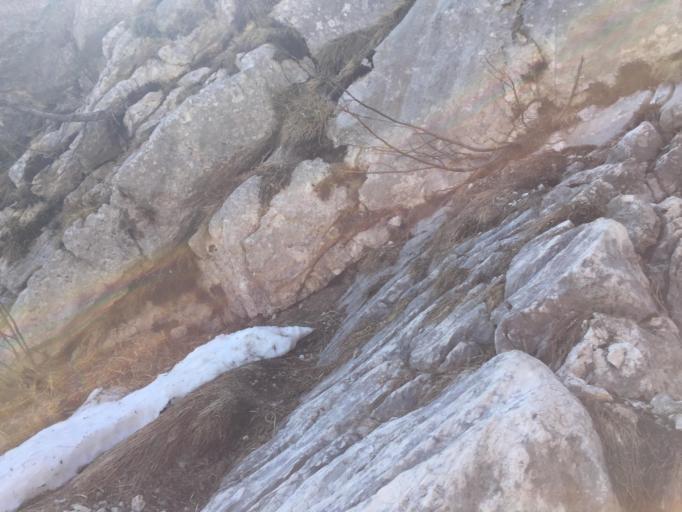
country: IT
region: Friuli Venezia Giulia
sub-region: Provincia di Udine
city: Amaro
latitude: 46.3983
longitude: 13.0812
